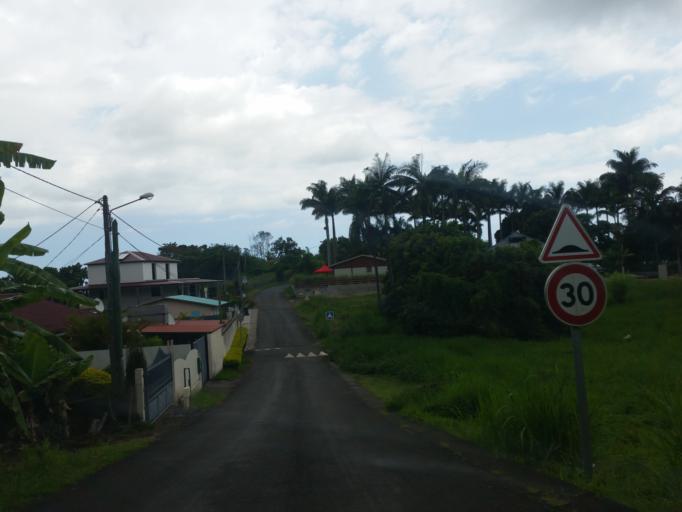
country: RE
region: Reunion
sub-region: Reunion
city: L'Entre-Deux
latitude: -21.2405
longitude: 55.4689
